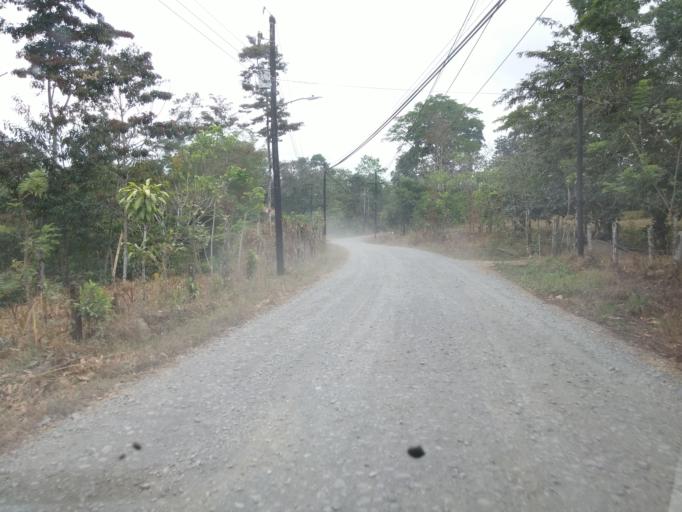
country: CR
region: Alajuela
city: Quesada
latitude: 10.3114
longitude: -84.5233
